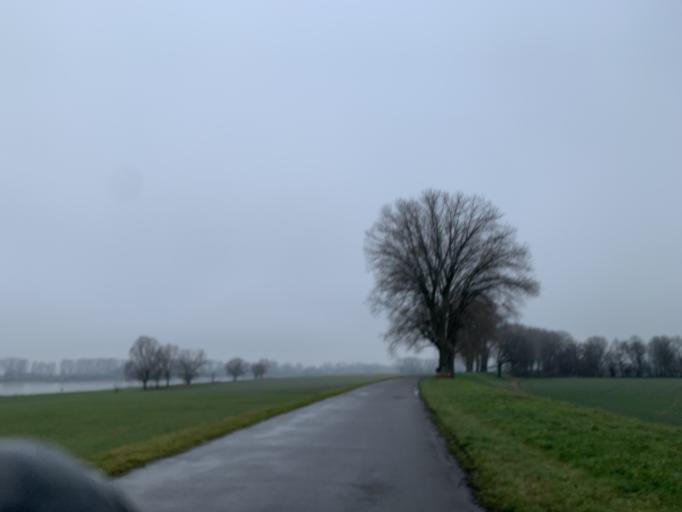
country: DE
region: North Rhine-Westphalia
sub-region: Regierungsbezirk Dusseldorf
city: Meerbusch
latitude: 51.2651
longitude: 6.7128
